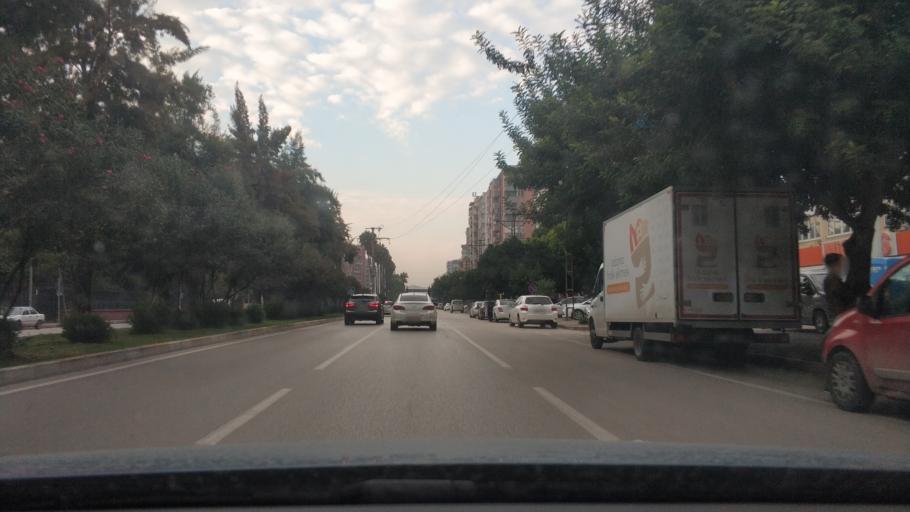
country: TR
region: Adana
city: Adana
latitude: 36.9992
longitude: 35.3167
